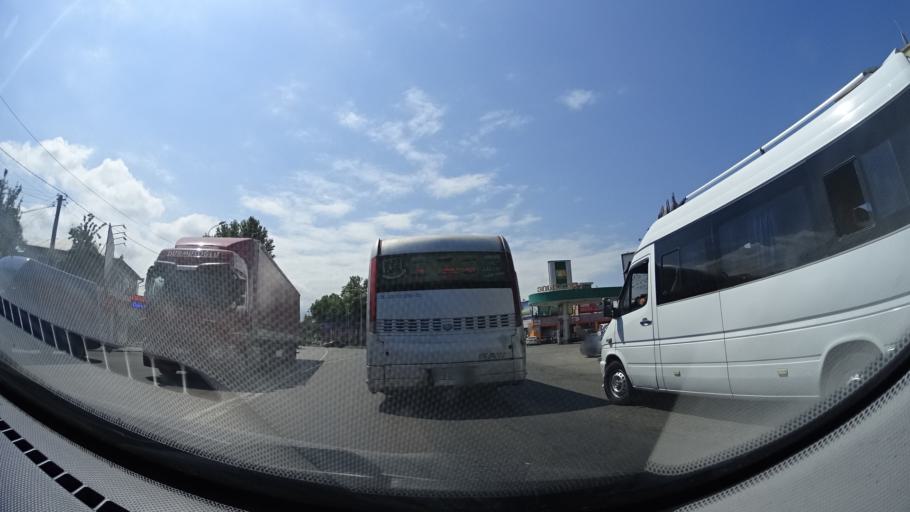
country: GE
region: Ajaria
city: Batumi
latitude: 41.6255
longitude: 41.6117
